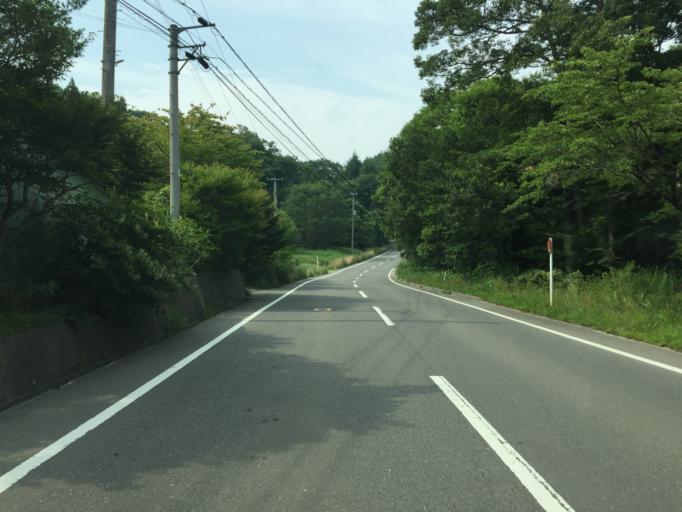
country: JP
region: Fukushima
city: Funehikimachi-funehiki
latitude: 37.4964
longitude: 140.7668
